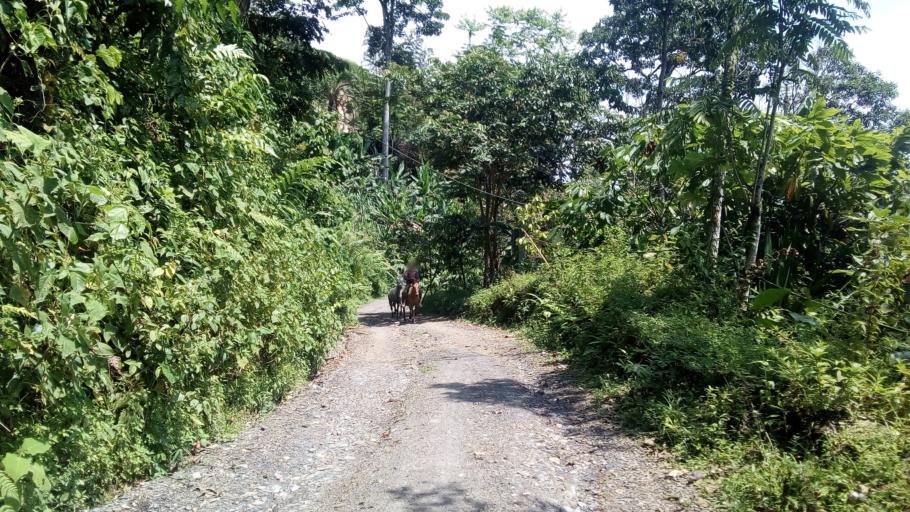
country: CO
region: Boyaca
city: Otanche
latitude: 5.6262
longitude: -74.2387
